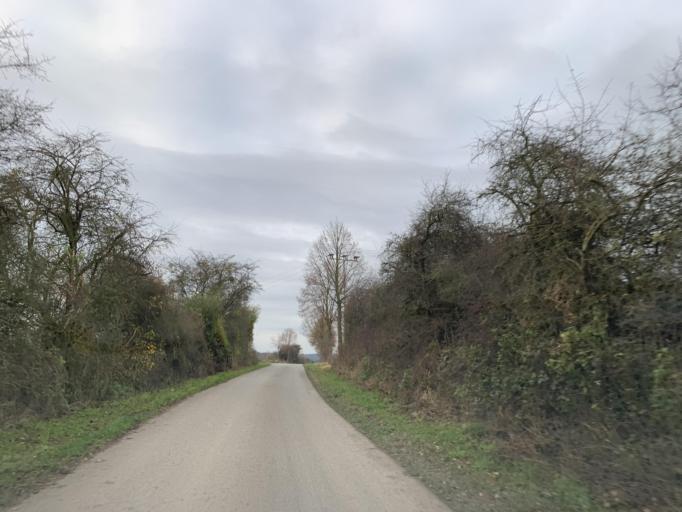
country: DE
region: Mecklenburg-Vorpommern
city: Carpin
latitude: 53.3995
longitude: 13.2081
